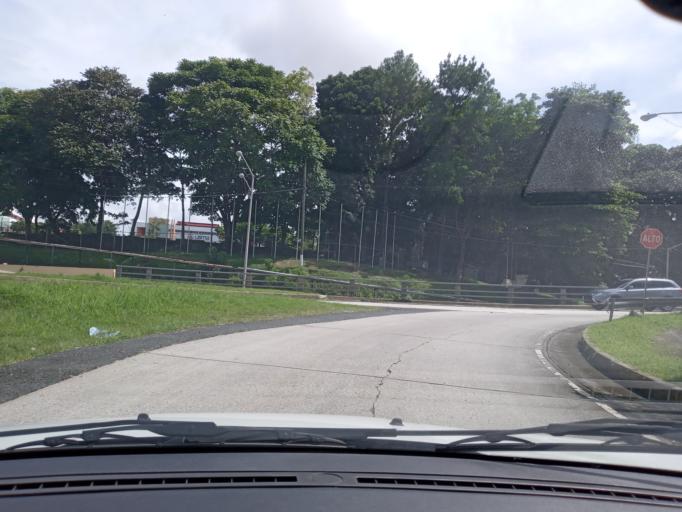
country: PA
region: Panama
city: Panama
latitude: 9.0276
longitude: -79.5206
